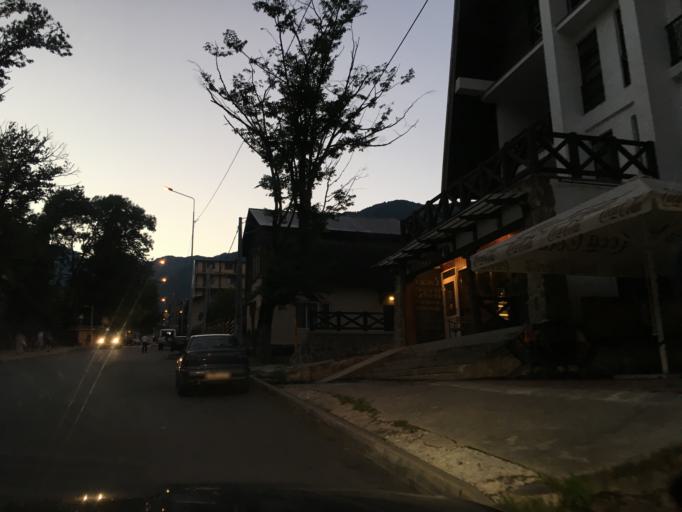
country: RU
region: Krasnodarskiy
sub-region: Sochi City
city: Krasnaya Polyana
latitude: 43.6774
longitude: 40.2067
